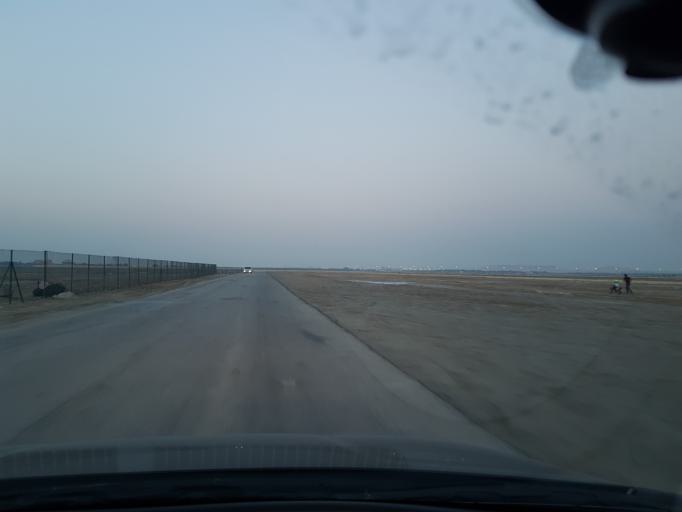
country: BH
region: Central Governorate
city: Dar Kulayb
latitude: 25.9995
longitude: 50.4713
